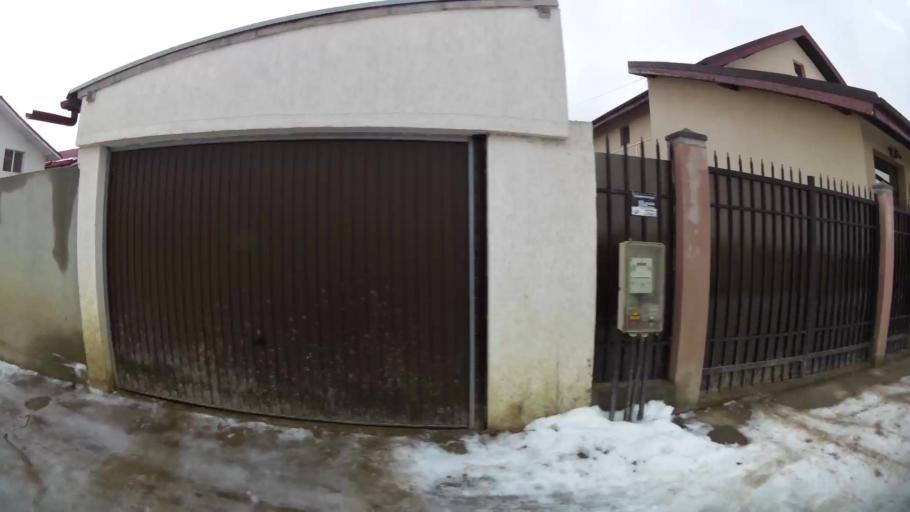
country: RO
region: Ilfov
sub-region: Comuna Pantelimon
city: Pantelimon
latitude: 44.4542
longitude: 26.2192
